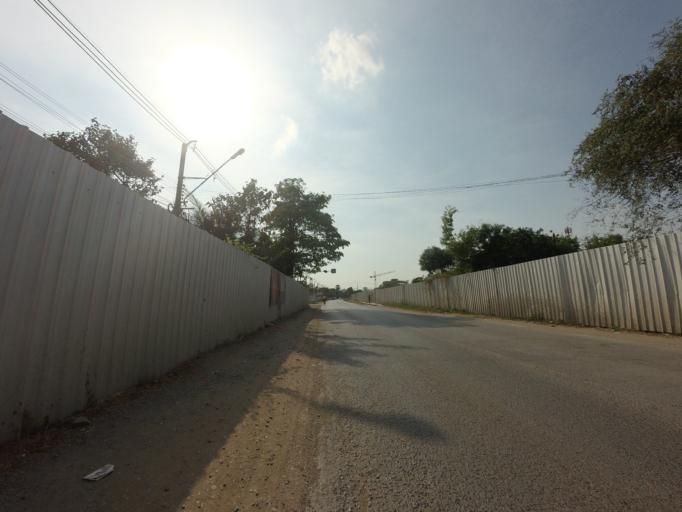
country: TH
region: Bangkok
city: Suan Luang
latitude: 13.7462
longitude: 100.6649
